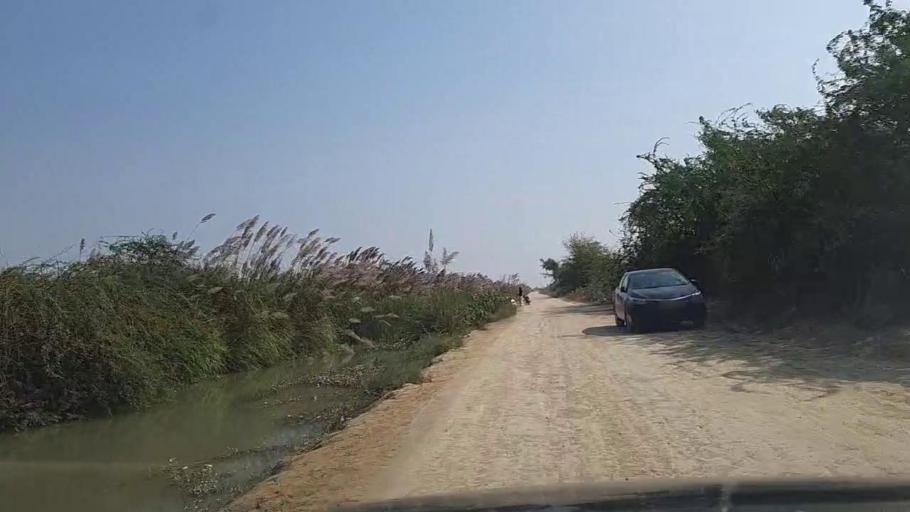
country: PK
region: Sindh
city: Gharo
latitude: 24.7203
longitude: 67.5583
